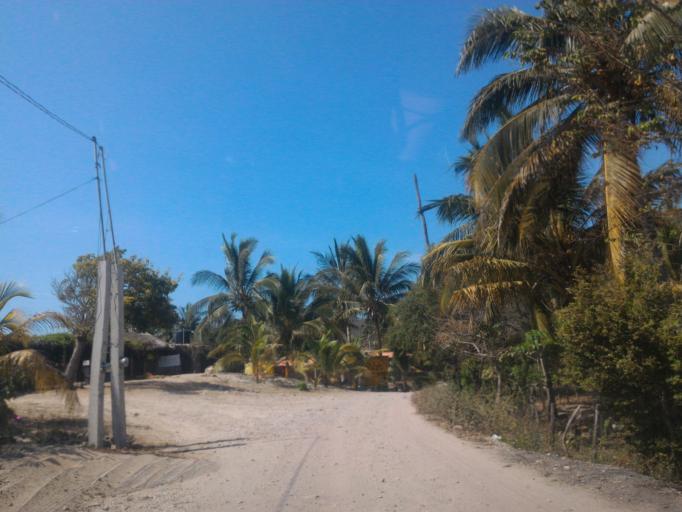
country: MX
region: Michoacan
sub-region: Coalcoman de Vazquez Pallares
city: Coalcoman de Vazquez Pallares
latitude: 18.2716
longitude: -103.3448
